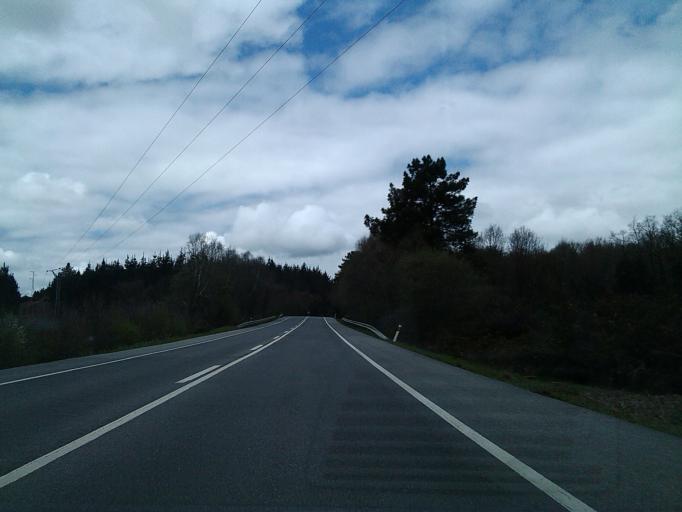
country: ES
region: Galicia
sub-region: Provincia de Lugo
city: Guitiriz
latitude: 43.1746
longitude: -7.8006
